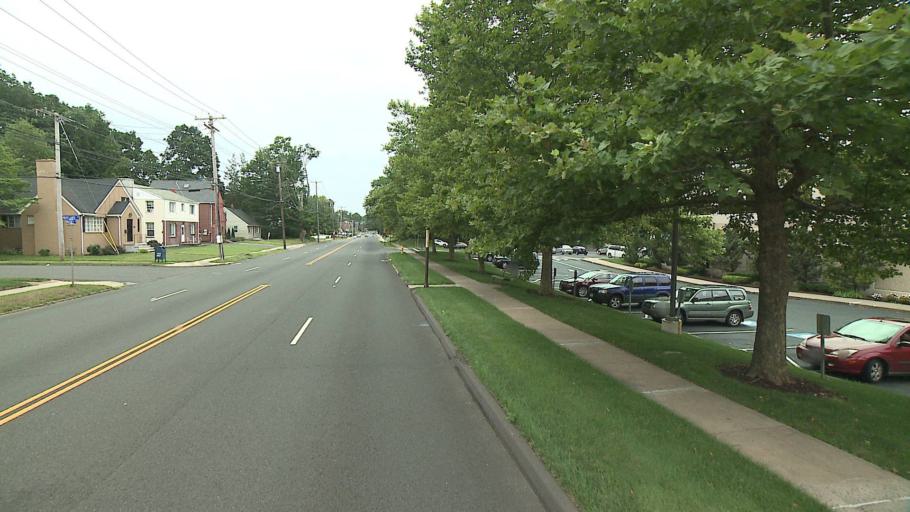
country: US
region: Connecticut
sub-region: New Haven County
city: Hamden
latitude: 41.3741
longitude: -72.9053
